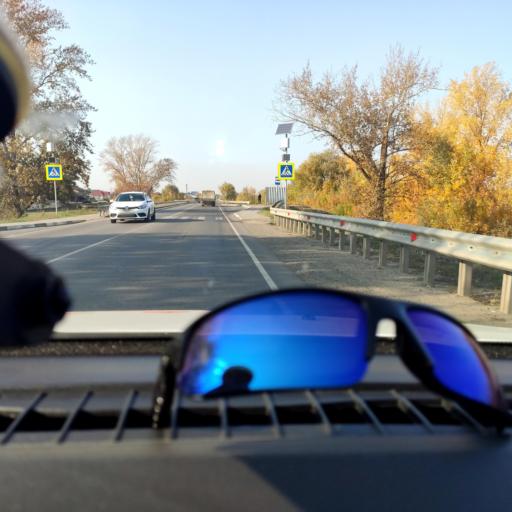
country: RU
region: Samara
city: Samara
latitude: 53.1167
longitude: 50.1235
